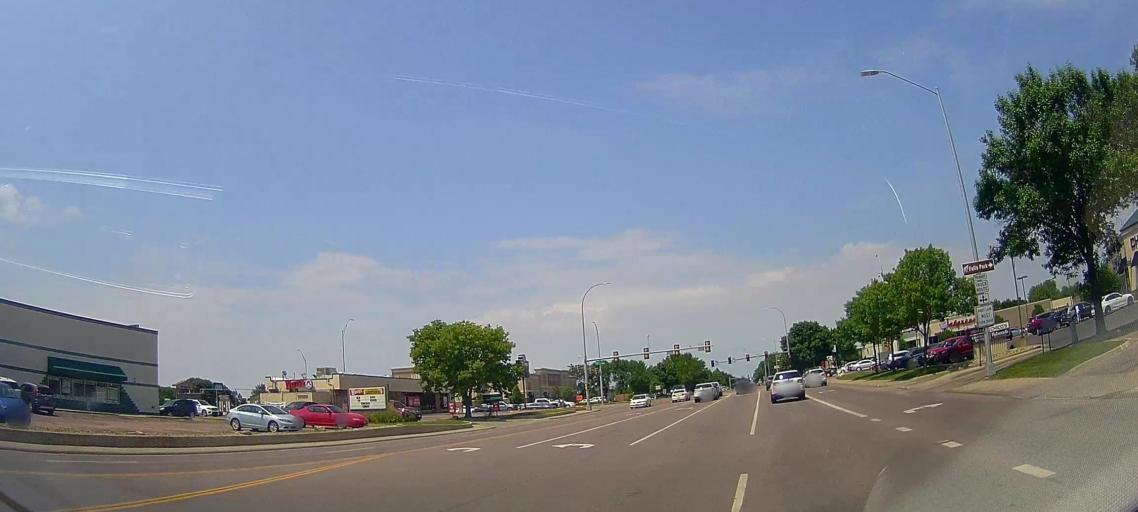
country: US
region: South Dakota
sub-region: Minnehaha County
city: Sioux Falls
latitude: 43.5140
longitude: -96.7710
